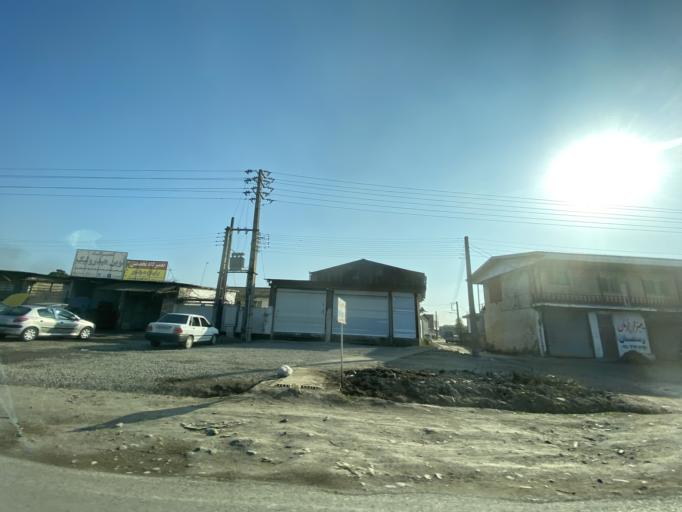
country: IR
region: Mazandaran
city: Babol
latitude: 36.5300
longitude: 52.6340
